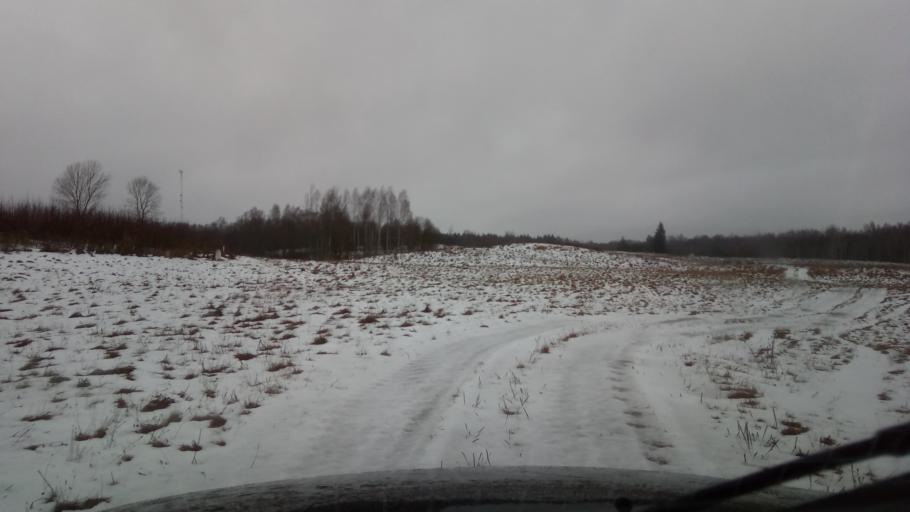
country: LT
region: Utenos apskritis
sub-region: Utena
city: Utena
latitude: 55.3645
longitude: 25.8094
